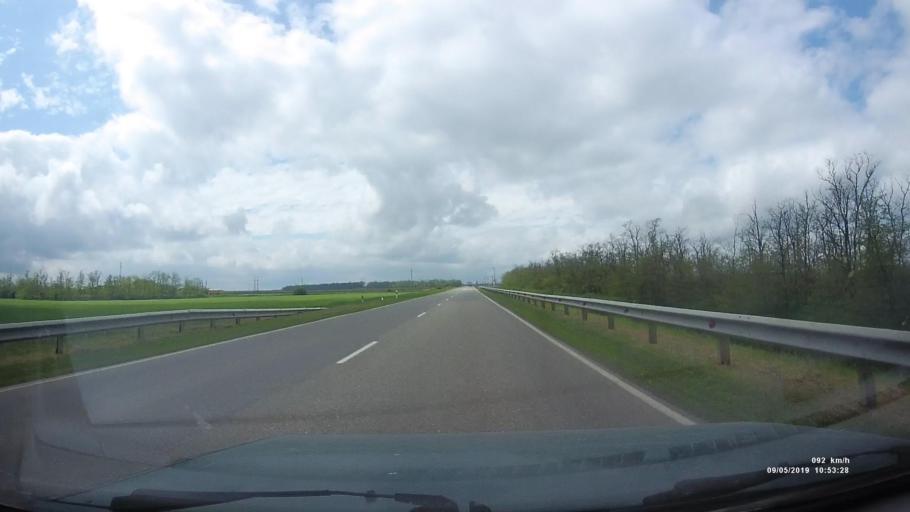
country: RU
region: Rostov
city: Peshkovo
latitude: 46.8888
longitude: 39.3419
